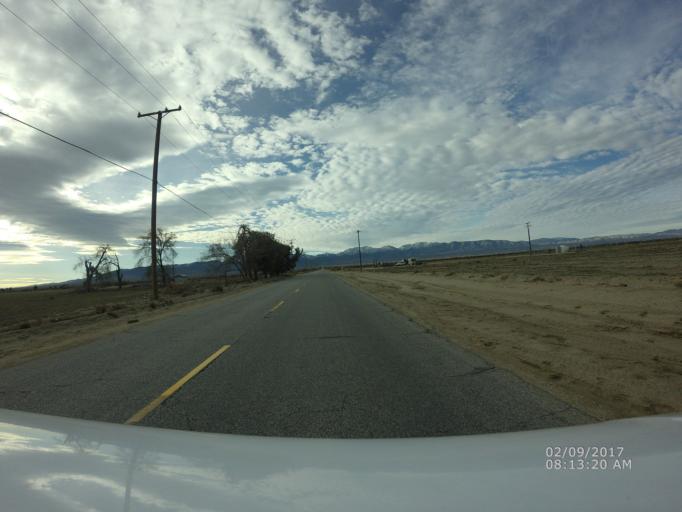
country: US
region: California
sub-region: Los Angeles County
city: Lake Los Angeles
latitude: 34.5660
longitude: -117.8357
